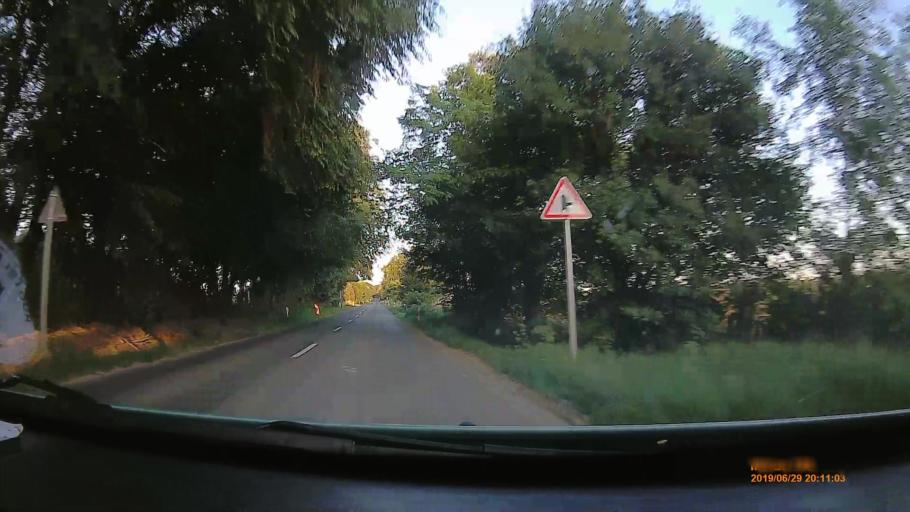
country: HU
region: Pest
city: Paty
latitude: 47.5303
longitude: 18.7857
